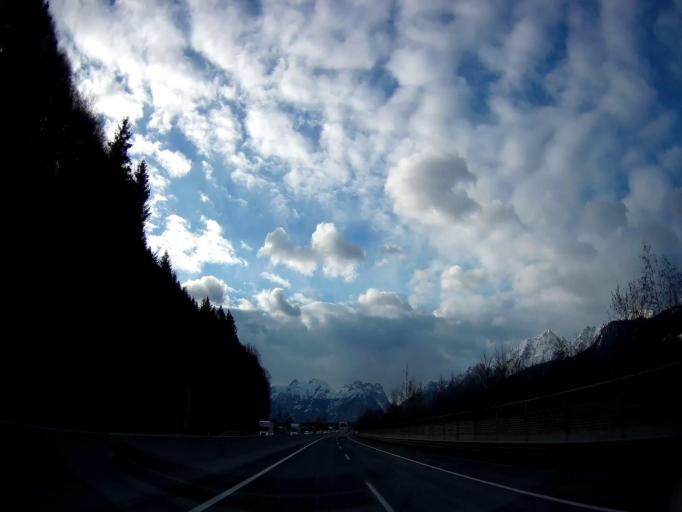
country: AT
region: Salzburg
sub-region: Politischer Bezirk Hallein
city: Adnet
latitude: 47.6811
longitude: 13.1214
